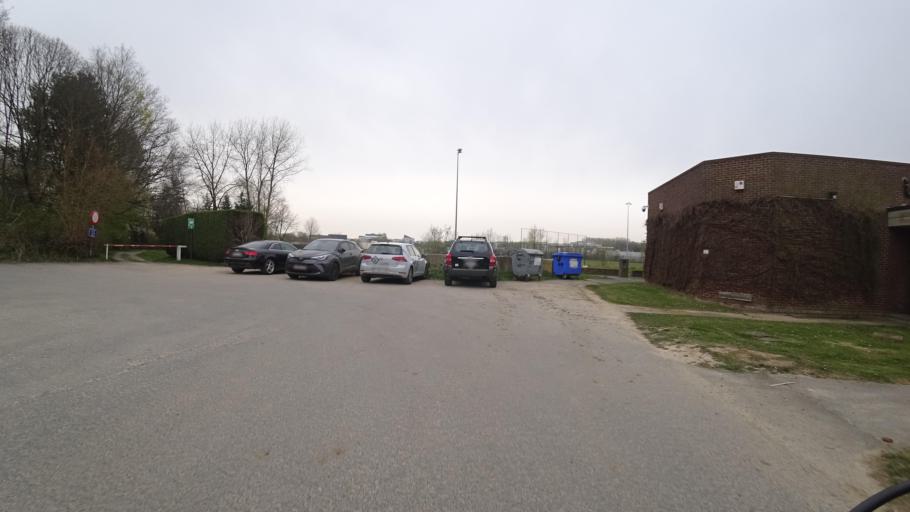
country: BE
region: Wallonia
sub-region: Province du Brabant Wallon
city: Louvain-la-Neuve
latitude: 50.6628
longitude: 4.6238
